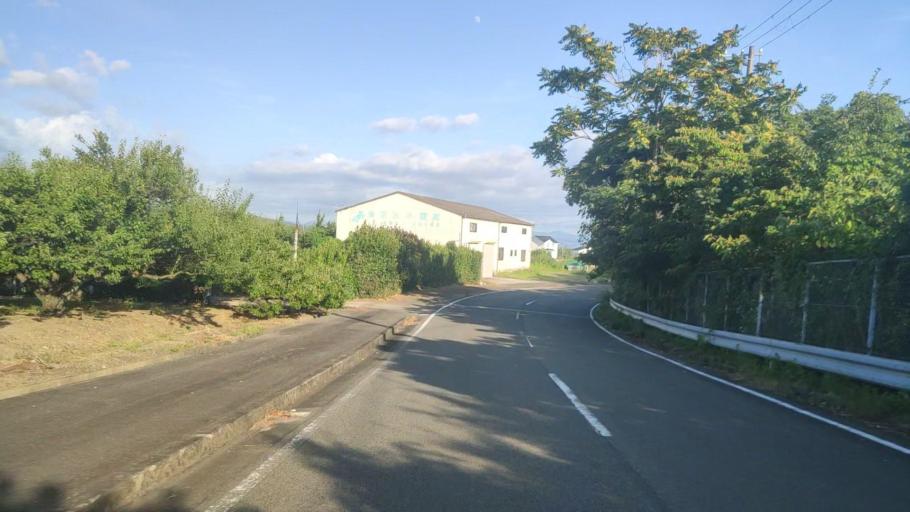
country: JP
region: Wakayama
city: Tanabe
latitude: 33.7769
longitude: 135.3035
